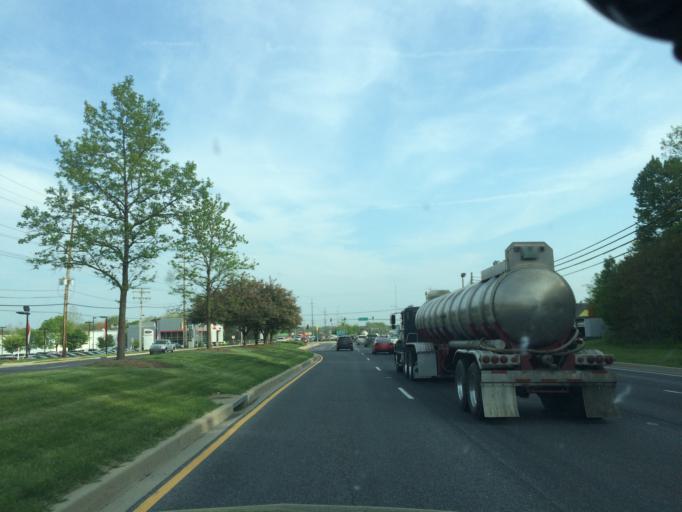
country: US
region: Maryland
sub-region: Carroll County
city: Westminster
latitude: 39.5712
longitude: -76.9826
